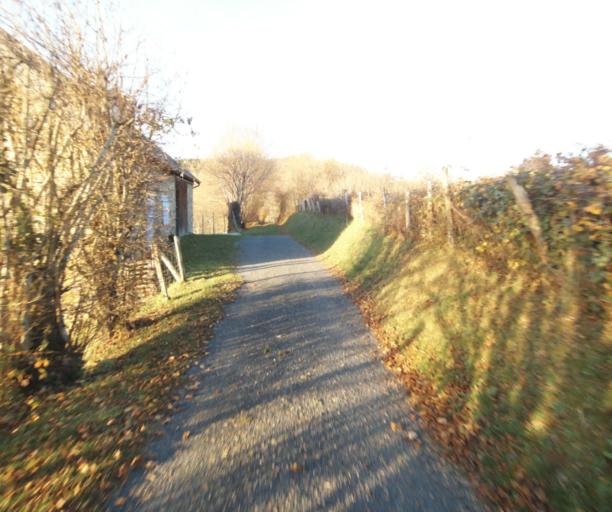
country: FR
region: Limousin
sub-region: Departement de la Correze
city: Laguenne
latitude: 45.2448
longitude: 1.8180
